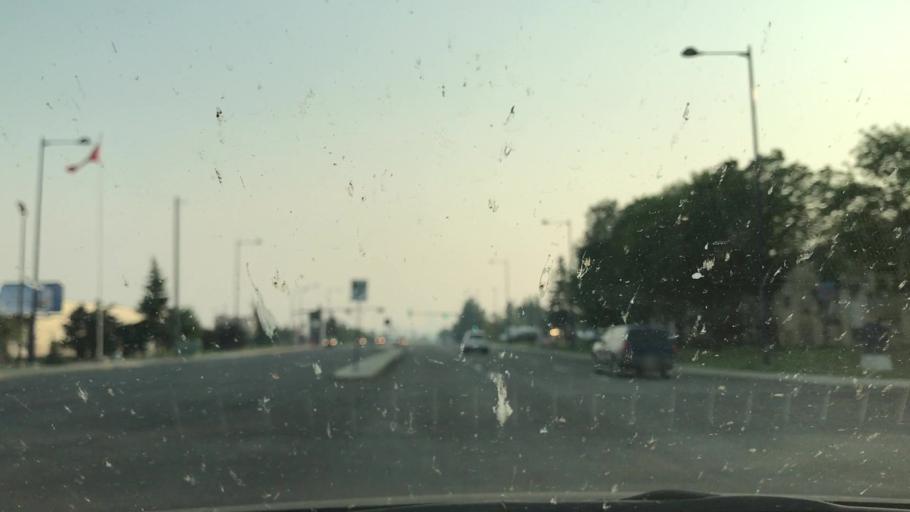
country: CA
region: Alberta
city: Edmonton
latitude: 53.5934
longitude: -113.4291
